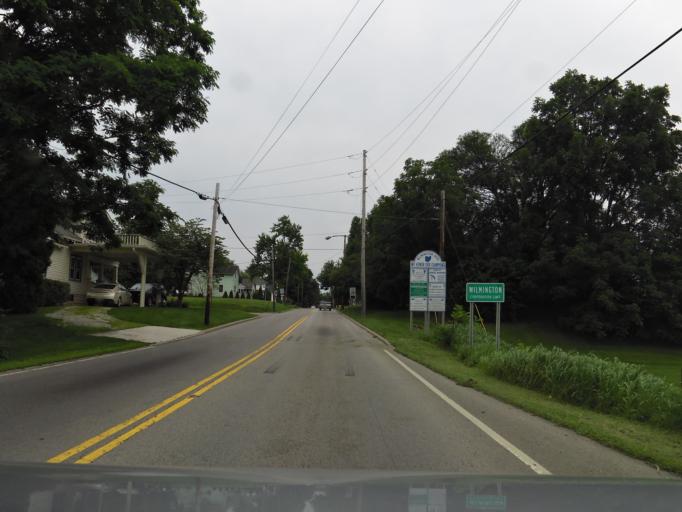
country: US
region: Ohio
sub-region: Clinton County
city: Wilmington
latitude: 39.4584
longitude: -83.8344
